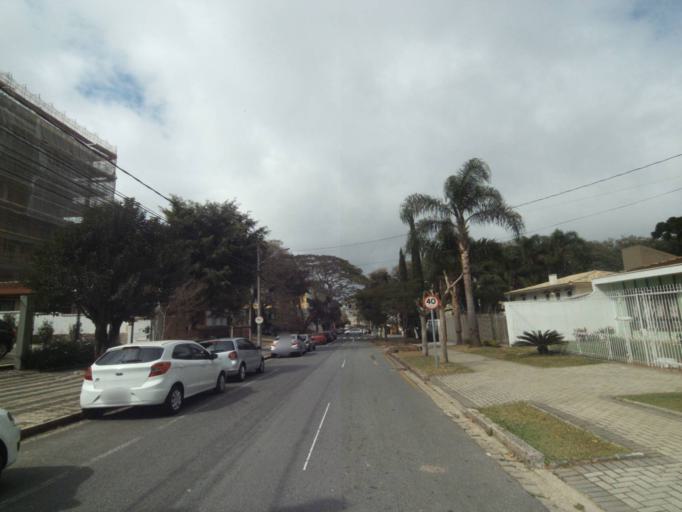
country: BR
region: Parana
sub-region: Curitiba
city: Curitiba
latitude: -25.4525
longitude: -49.2936
